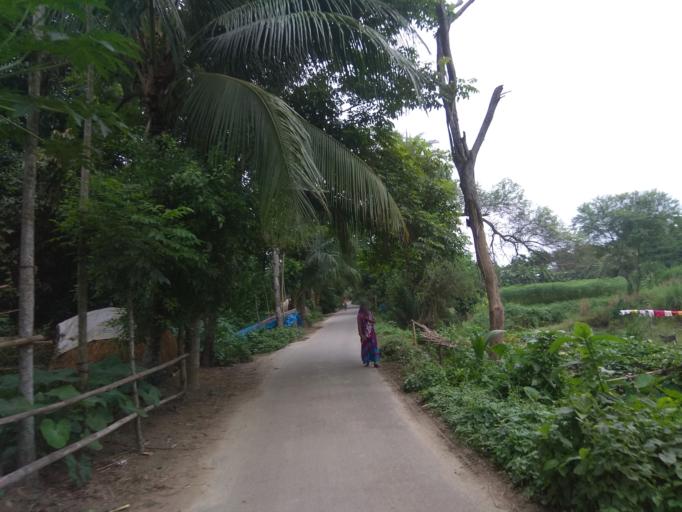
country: BD
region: Dhaka
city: Dohar
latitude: 23.4838
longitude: 90.0076
